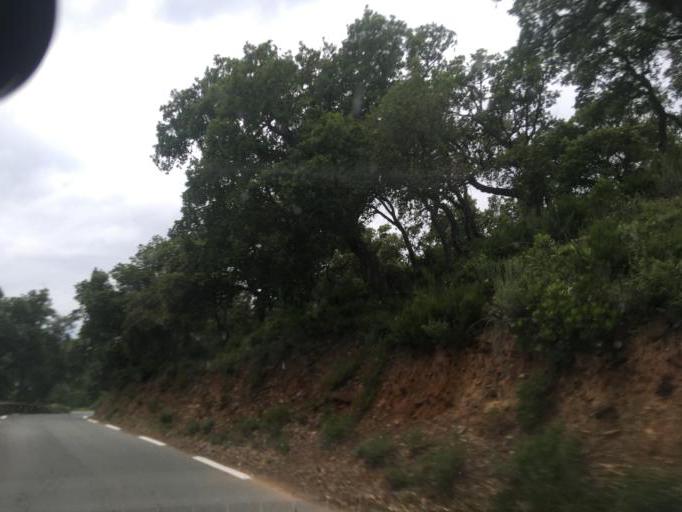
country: FR
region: Provence-Alpes-Cote d'Azur
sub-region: Departement du Var
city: Pierrefeu-du-Var
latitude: 43.2127
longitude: 6.2169
